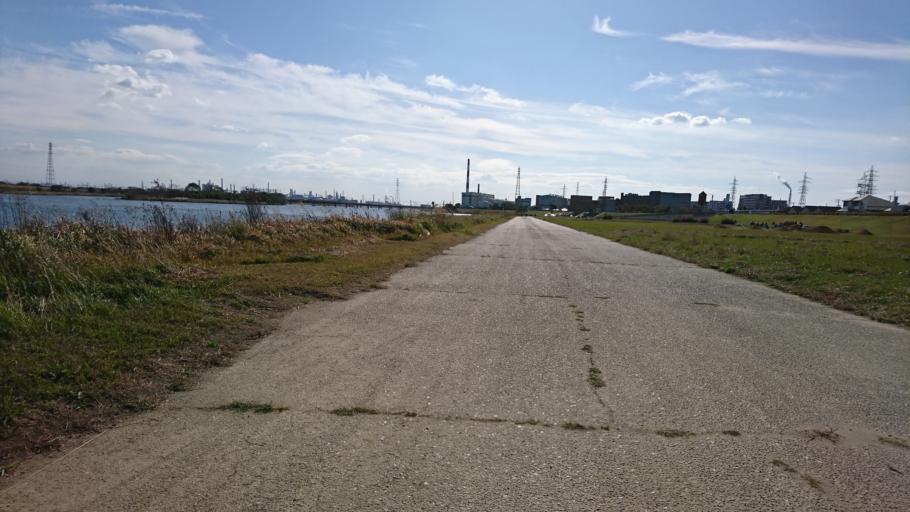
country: JP
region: Hyogo
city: Kakogawacho-honmachi
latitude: 34.7592
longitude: 134.8058
